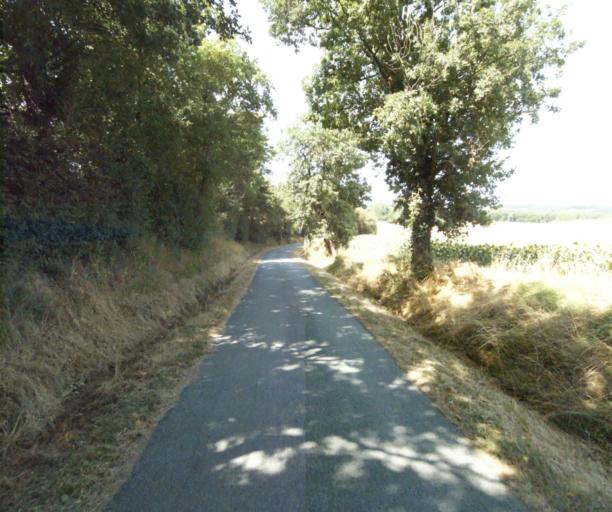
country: FR
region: Midi-Pyrenees
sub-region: Departement de la Haute-Garonne
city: Revel
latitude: 43.5107
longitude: 2.0298
